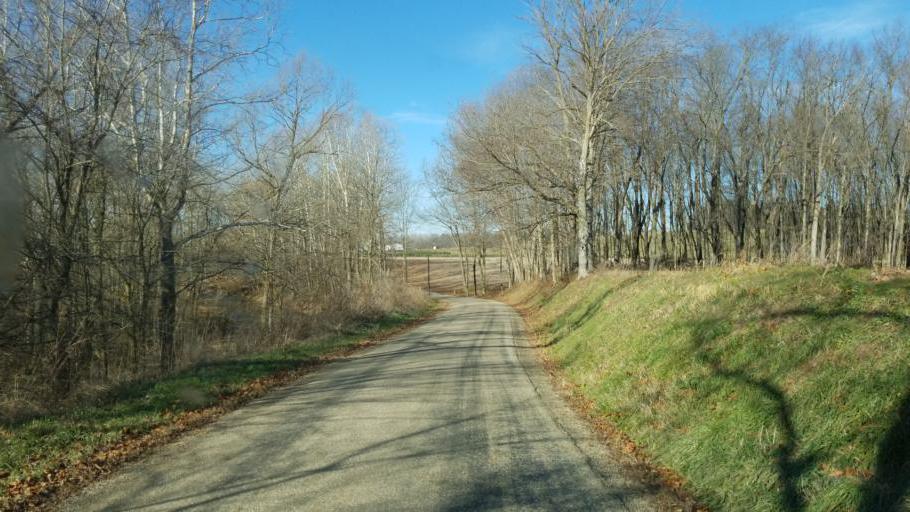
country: US
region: Ohio
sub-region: Richland County
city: Lexington
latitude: 40.6210
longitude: -82.5939
